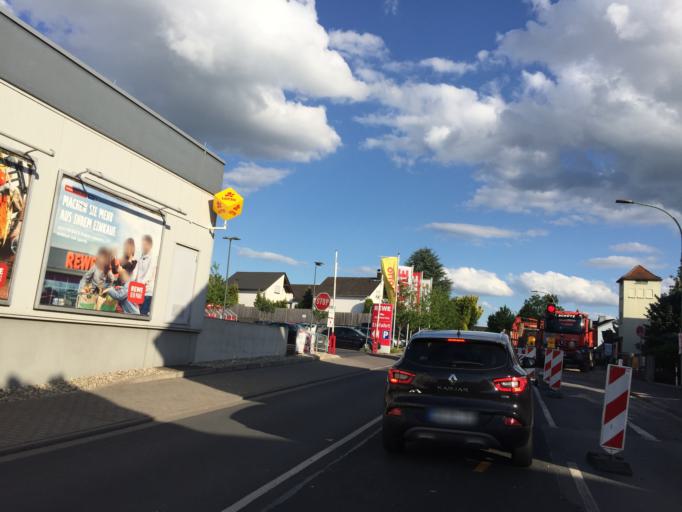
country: DE
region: Hesse
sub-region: Regierungsbezirk Darmstadt
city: Karben
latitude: 50.2216
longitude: 8.7767
